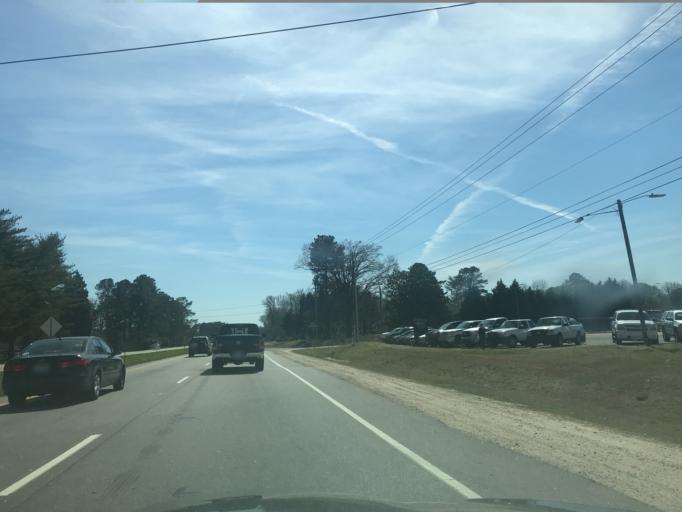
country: US
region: North Carolina
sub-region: Wake County
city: Garner
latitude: 35.6613
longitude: -78.7031
